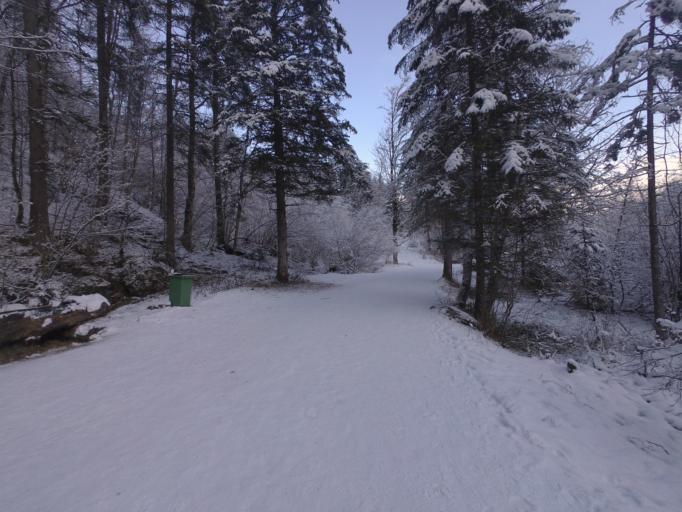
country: AT
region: Salzburg
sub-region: Politischer Bezirk Hallein
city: Golling an der Salzach
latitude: 47.5828
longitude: 13.1455
